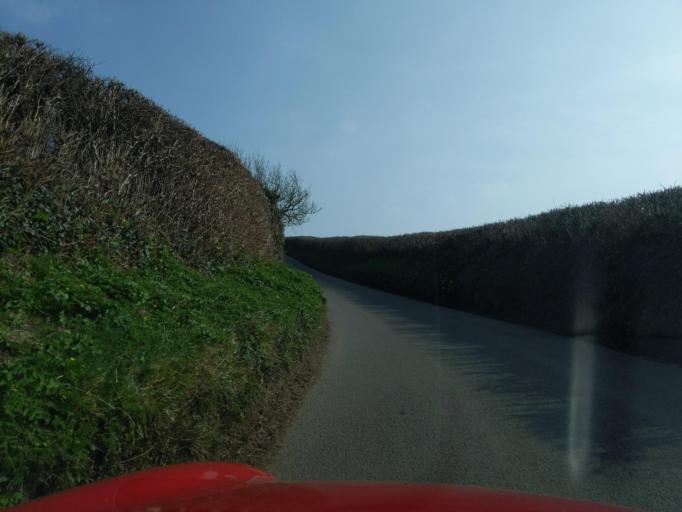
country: GB
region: England
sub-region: Devon
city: Salcombe
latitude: 50.2668
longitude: -3.7223
